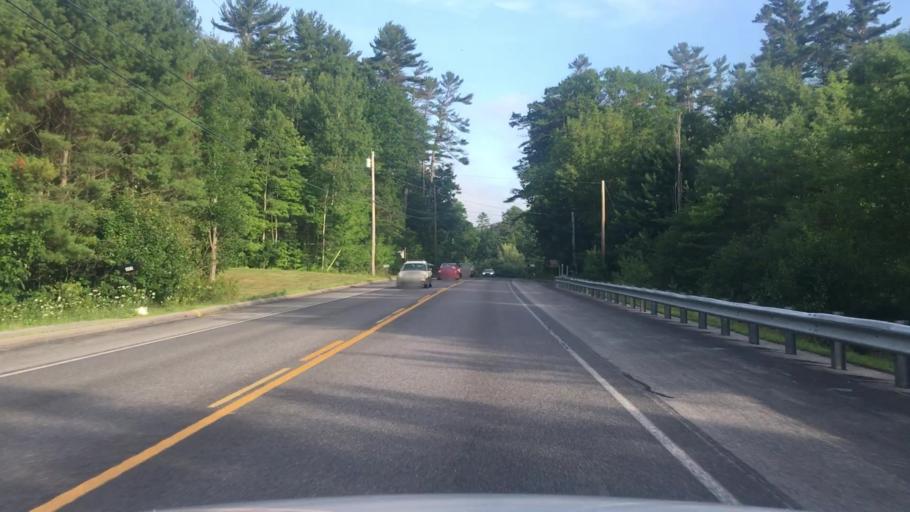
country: US
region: Maine
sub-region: Cumberland County
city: North Windham
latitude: 43.7947
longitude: -70.3994
